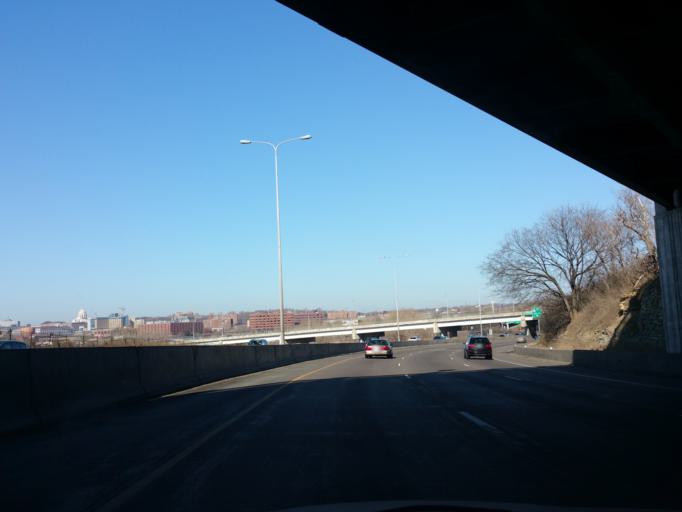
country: US
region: Minnesota
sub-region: Ramsey County
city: Saint Paul
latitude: 44.9523
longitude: -93.0700
